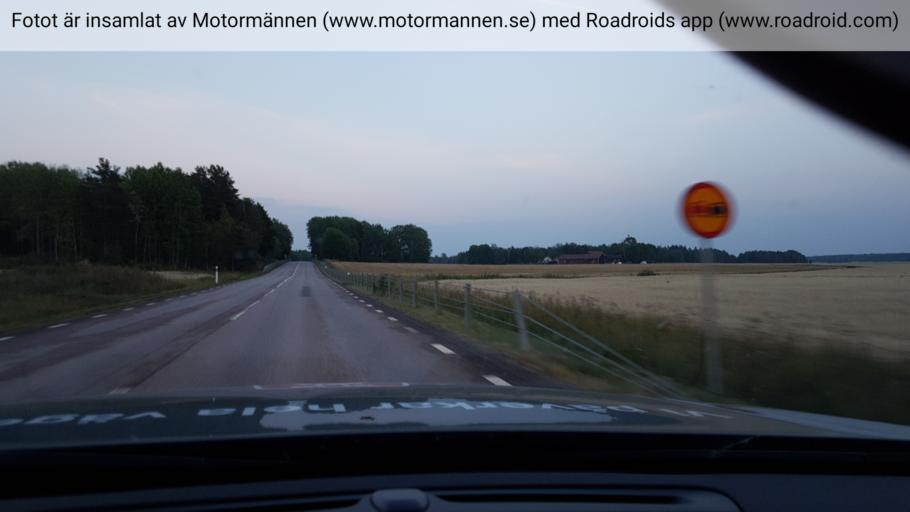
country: SE
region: Uppsala
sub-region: Heby Kommun
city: Heby
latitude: 59.8228
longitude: 16.7545
